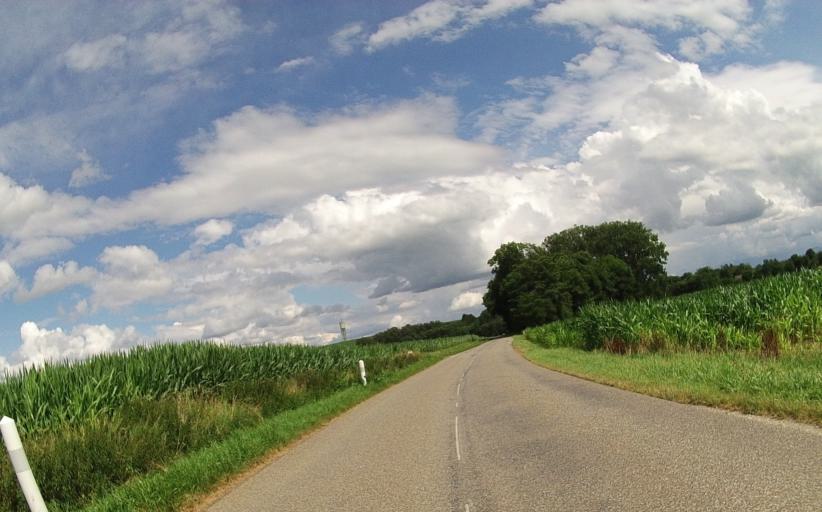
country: FR
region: Alsace
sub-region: Departement du Bas-Rhin
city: Roppenheim
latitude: 48.9152
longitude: 8.0256
